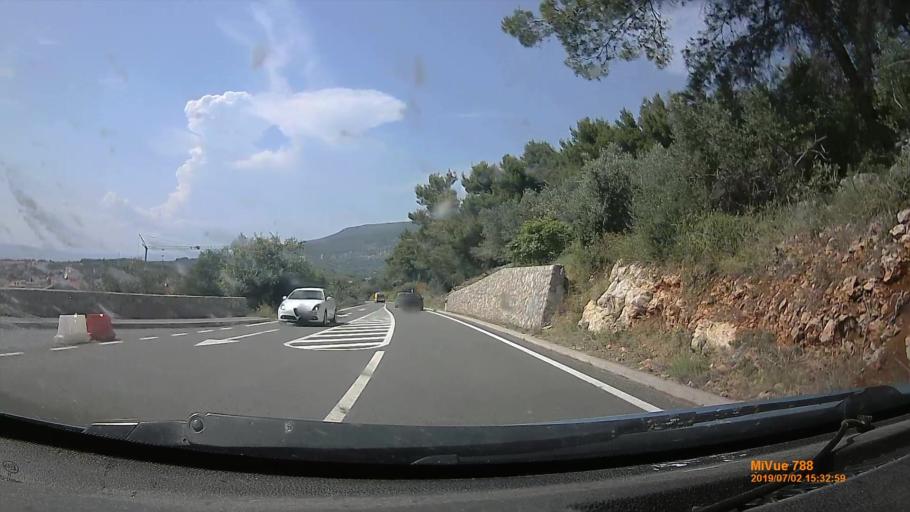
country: HR
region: Primorsko-Goranska
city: Cres
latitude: 44.9561
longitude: 14.4175
